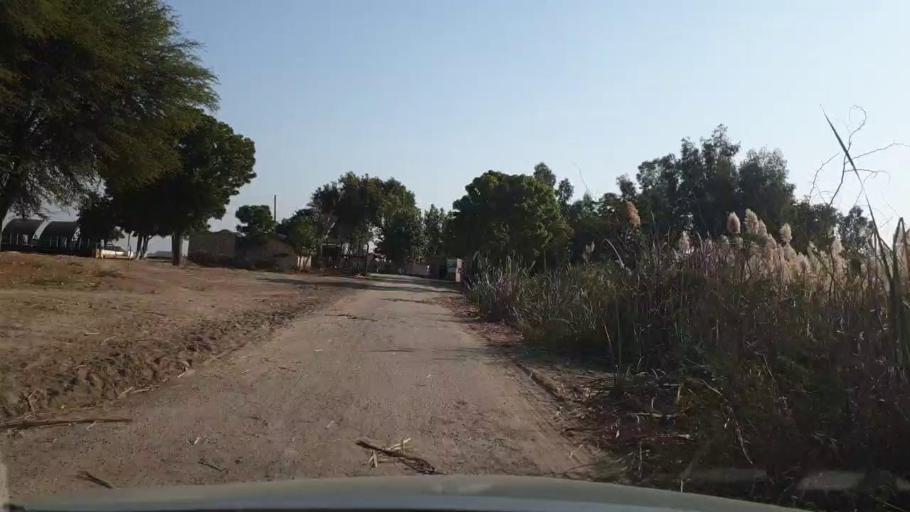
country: PK
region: Sindh
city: Tando Allahyar
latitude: 25.5942
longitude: 68.6275
